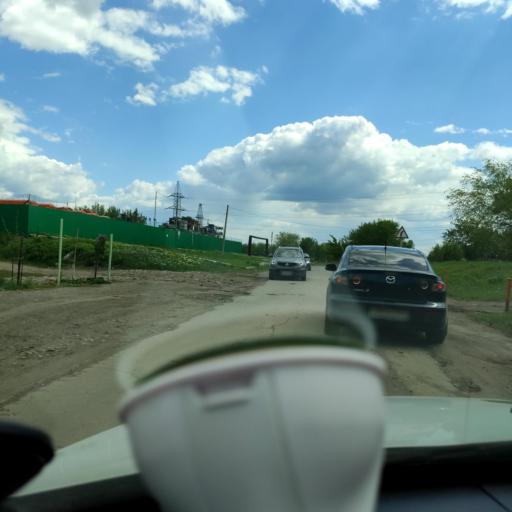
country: RU
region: Samara
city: Petra-Dubrava
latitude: 53.2656
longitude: 50.3161
